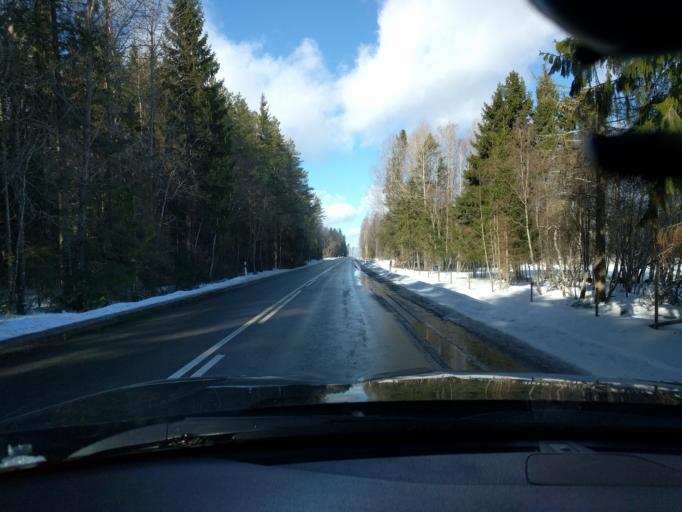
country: EE
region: Harju
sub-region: Raasiku vald
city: Raasiku
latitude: 59.2867
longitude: 25.1909
